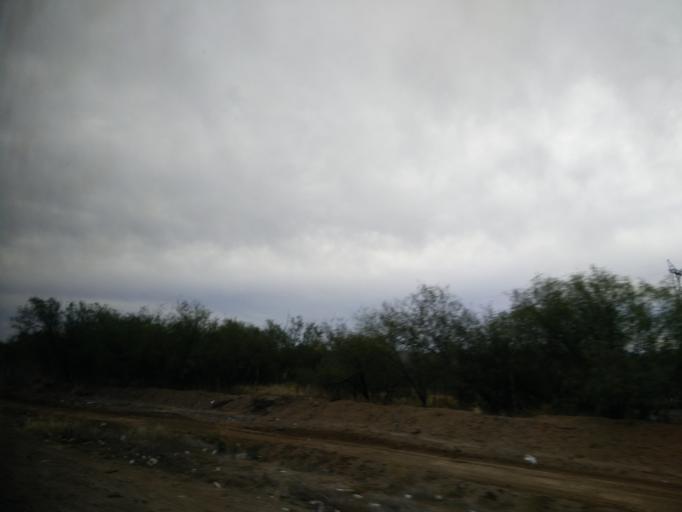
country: MX
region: Sonora
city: Hermosillo
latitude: 28.6820
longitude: -110.9921
